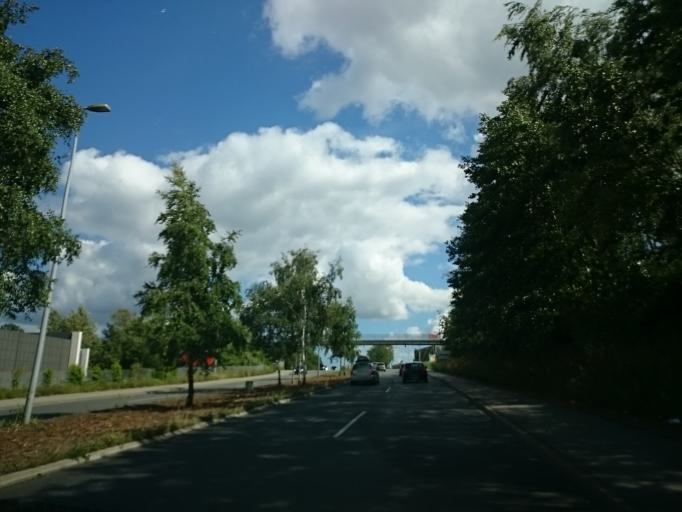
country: DK
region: Central Jutland
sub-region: Arhus Kommune
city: Stavtrup
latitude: 56.1151
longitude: 10.1510
